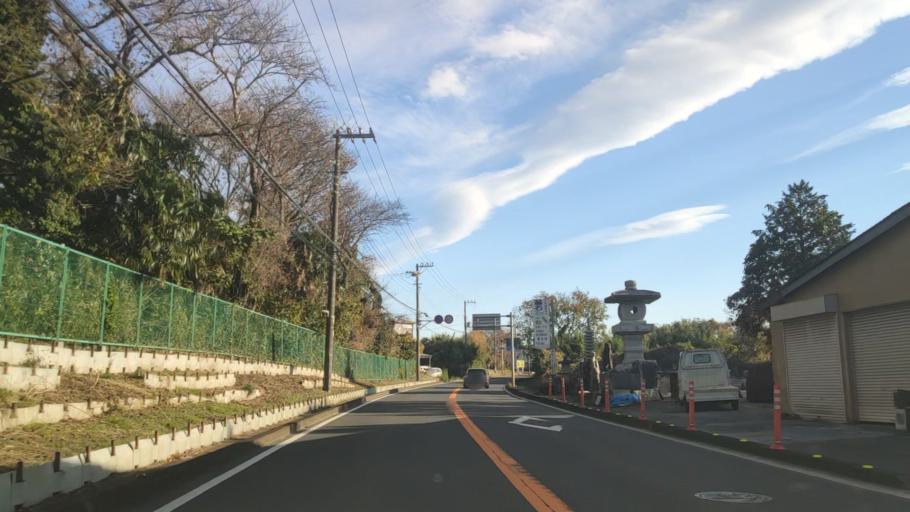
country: JP
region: Kanagawa
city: Atsugi
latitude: 35.4129
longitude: 139.4048
